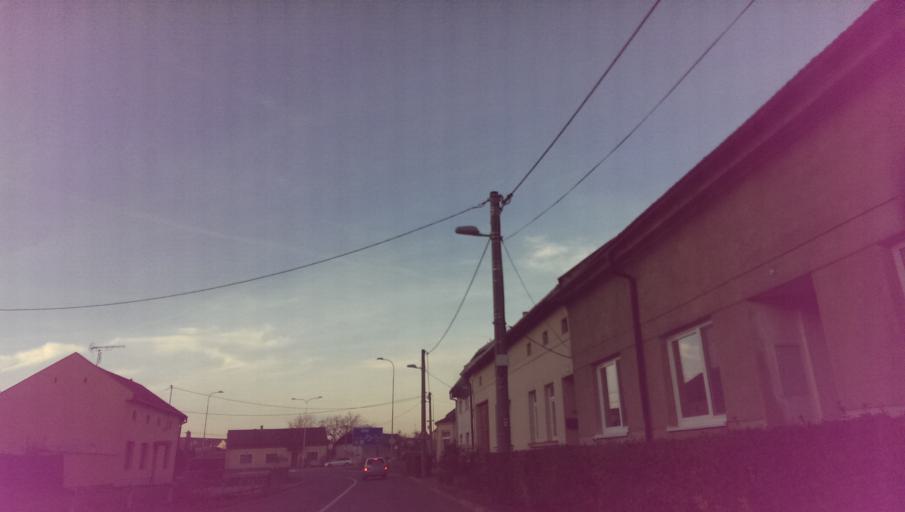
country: CZ
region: Zlin
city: Tecovice
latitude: 49.2063
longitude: 17.5968
